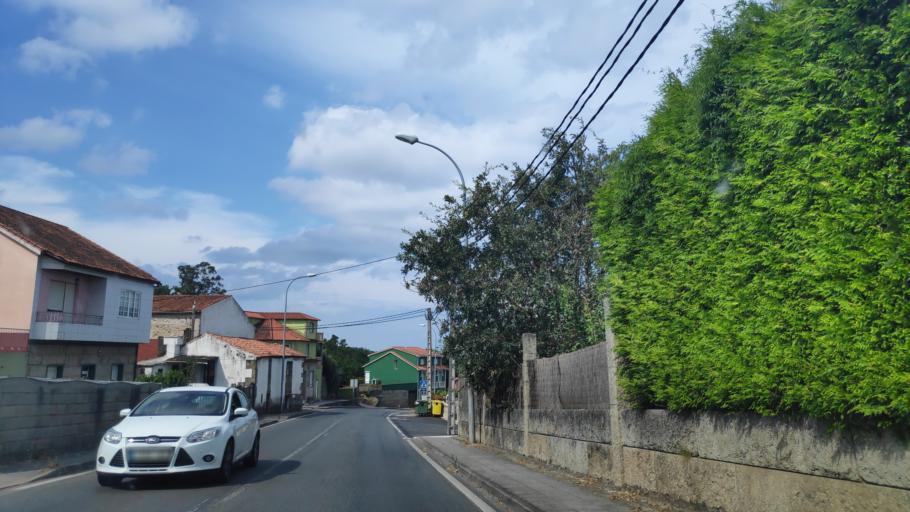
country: ES
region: Galicia
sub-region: Provincia de Pontevedra
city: Vilagarcia de Arousa
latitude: 42.5932
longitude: -8.7380
